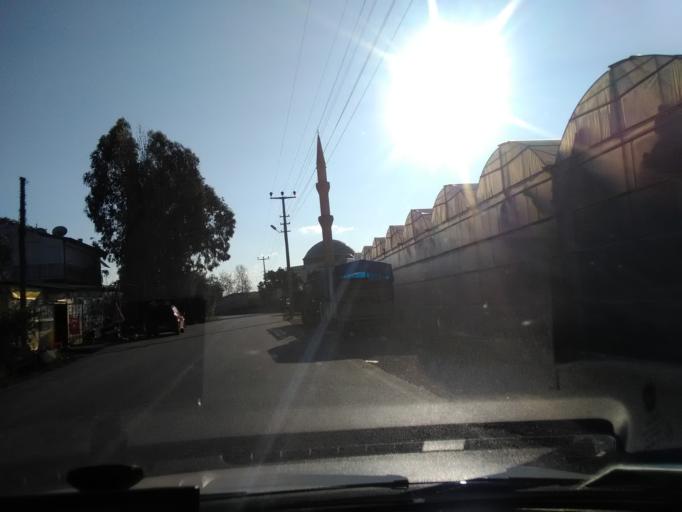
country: TR
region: Antalya
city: Gazipasa
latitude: 36.2512
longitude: 32.3031
